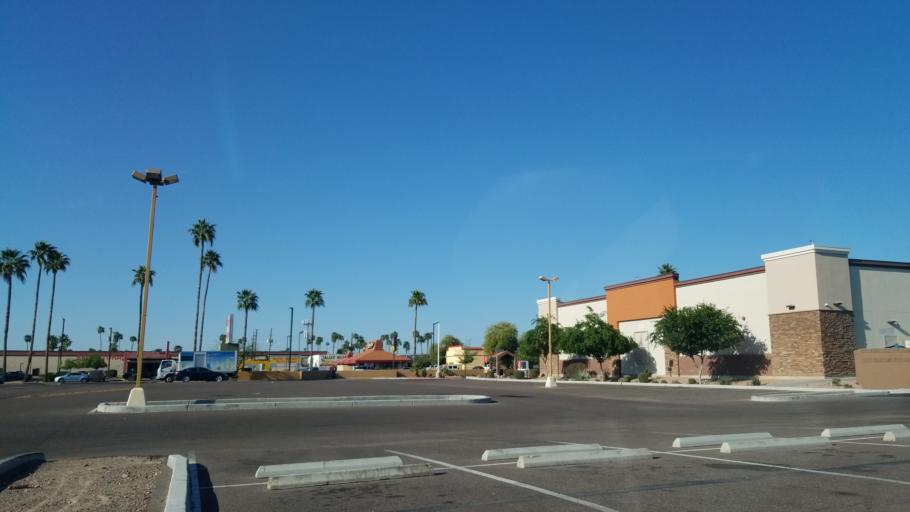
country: US
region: Arizona
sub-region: Maricopa County
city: Glendale
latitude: 33.5375
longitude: -112.1528
